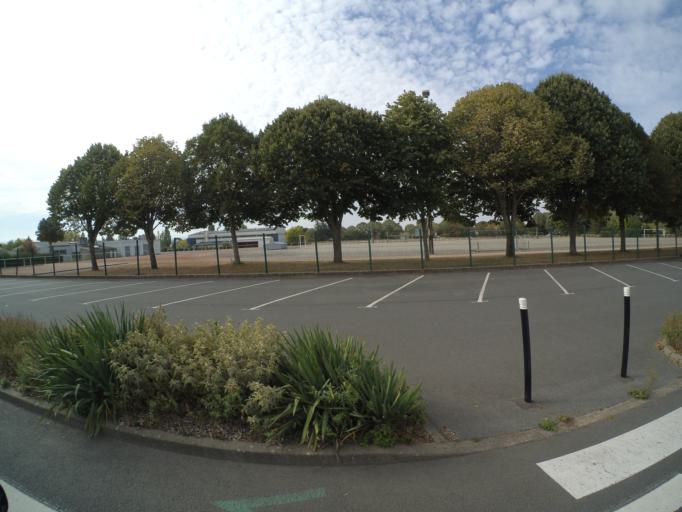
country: FR
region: Pays de la Loire
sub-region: Departement de Maine-et-Loire
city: Chemille-Melay
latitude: 47.2168
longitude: -0.7251
